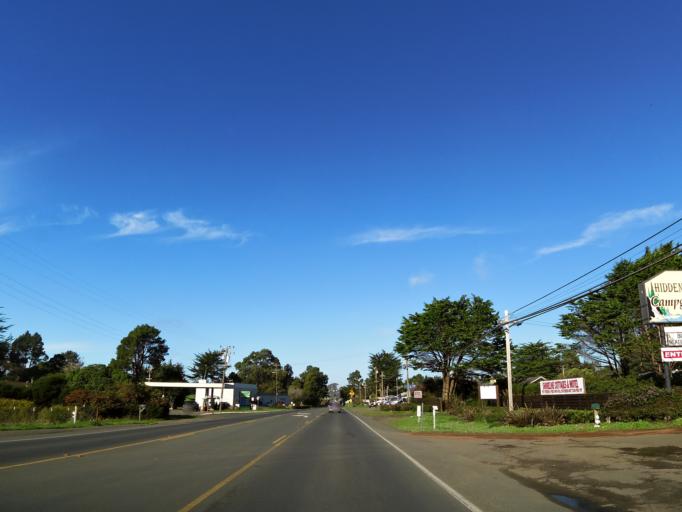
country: US
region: California
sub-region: Mendocino County
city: Fort Bragg
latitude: 39.4150
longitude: -123.8082
